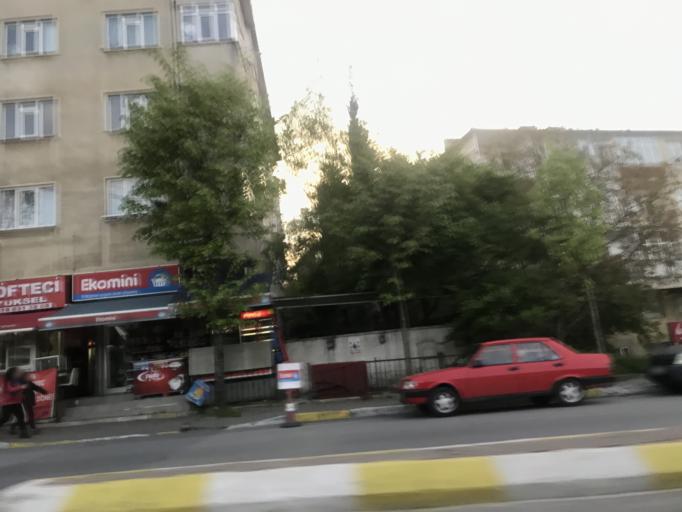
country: TR
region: Istanbul
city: Umraniye
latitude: 41.0325
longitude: 29.0963
